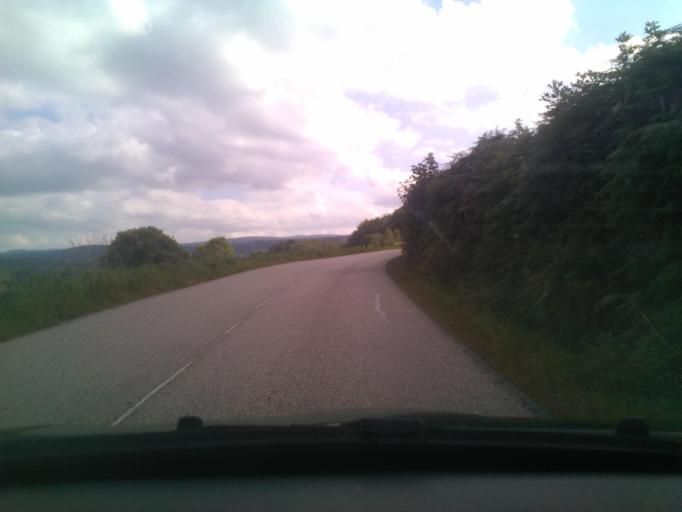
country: FR
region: Lorraine
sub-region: Departement des Vosges
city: Corcieux
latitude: 48.1522
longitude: 6.8634
